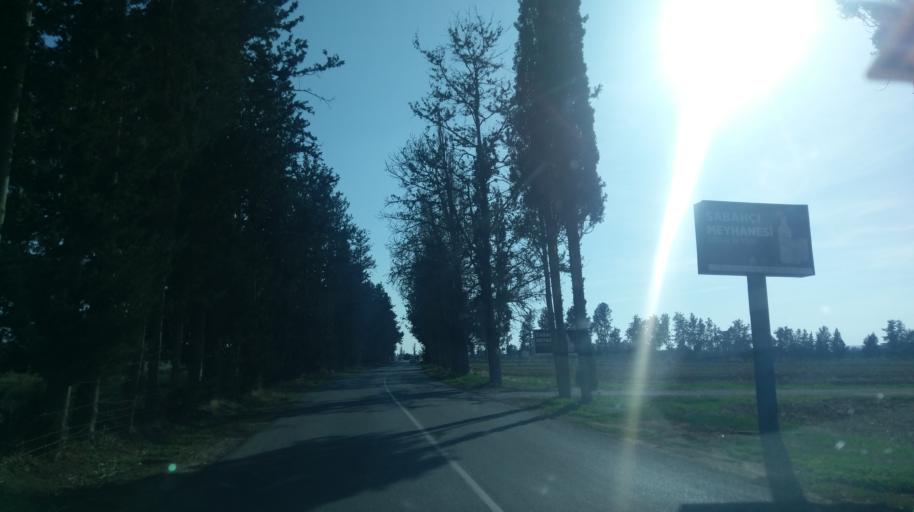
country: CY
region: Larnaka
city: Pergamos
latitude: 35.1066
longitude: 33.7284
